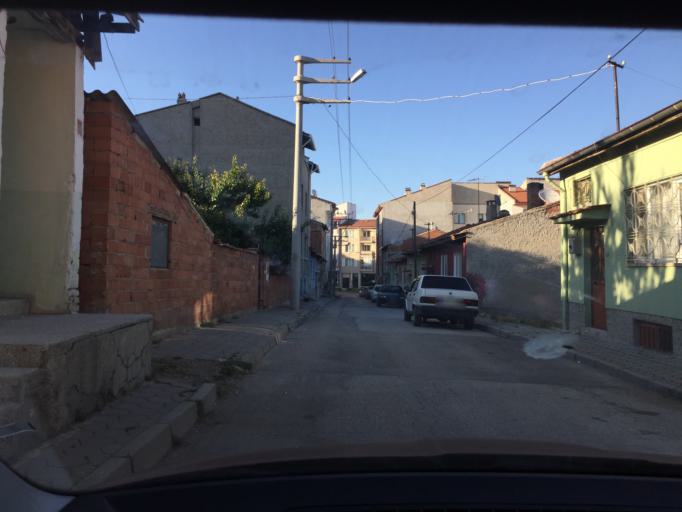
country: TR
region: Eskisehir
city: Eskisehir
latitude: 39.7777
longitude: 30.4531
